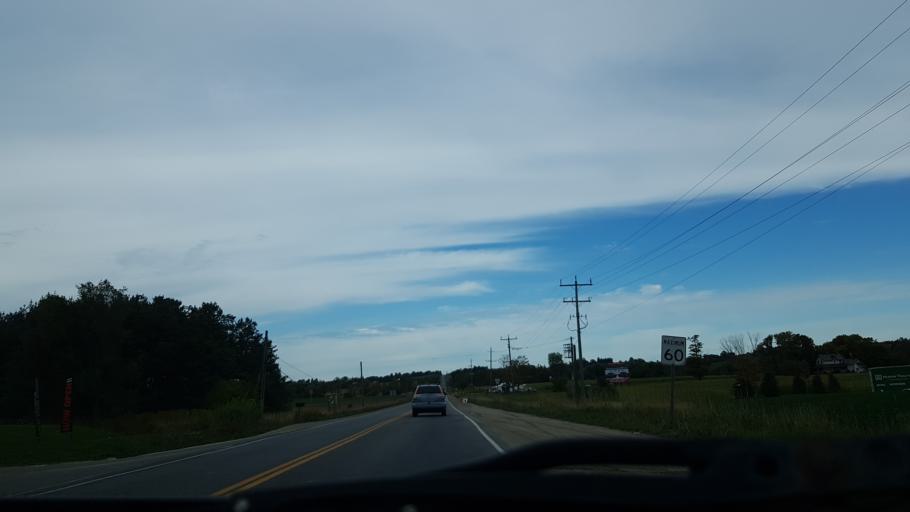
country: CA
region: Ontario
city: Wasaga Beach
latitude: 44.3373
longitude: -80.0784
